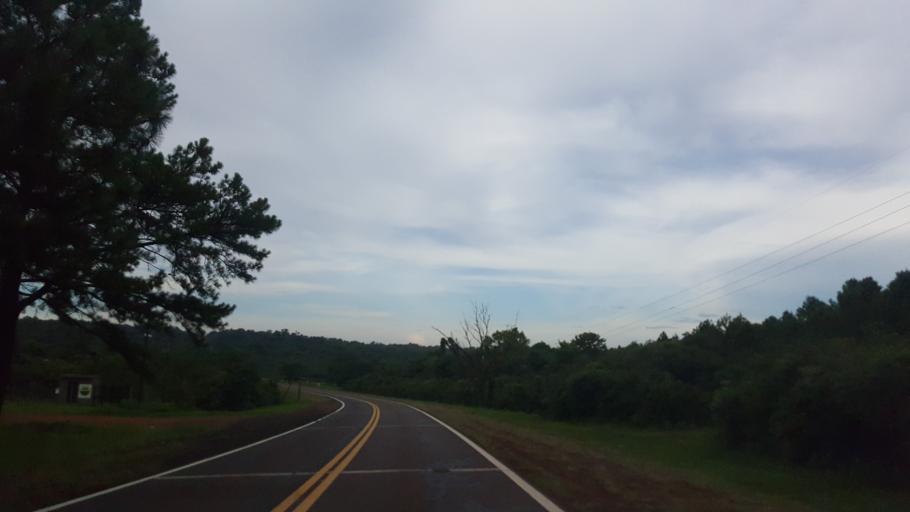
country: AR
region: Misiones
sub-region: Departamento de San Ignacio
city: San Ignacio
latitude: -27.2548
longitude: -55.5248
